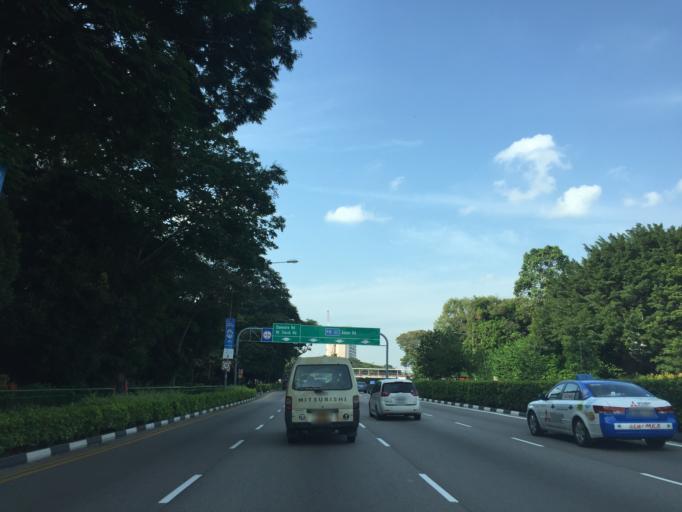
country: SG
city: Singapore
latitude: 1.3181
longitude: 103.8081
